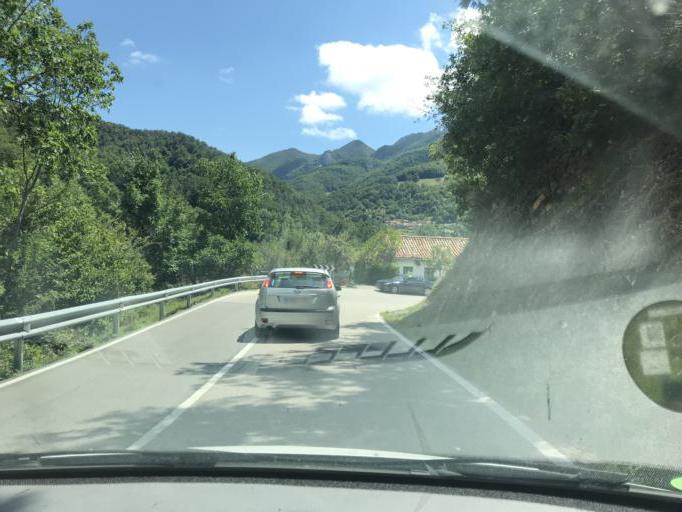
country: ES
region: Cantabria
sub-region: Provincia de Cantabria
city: Cabezon de Liebana
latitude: 43.0753
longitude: -4.4998
